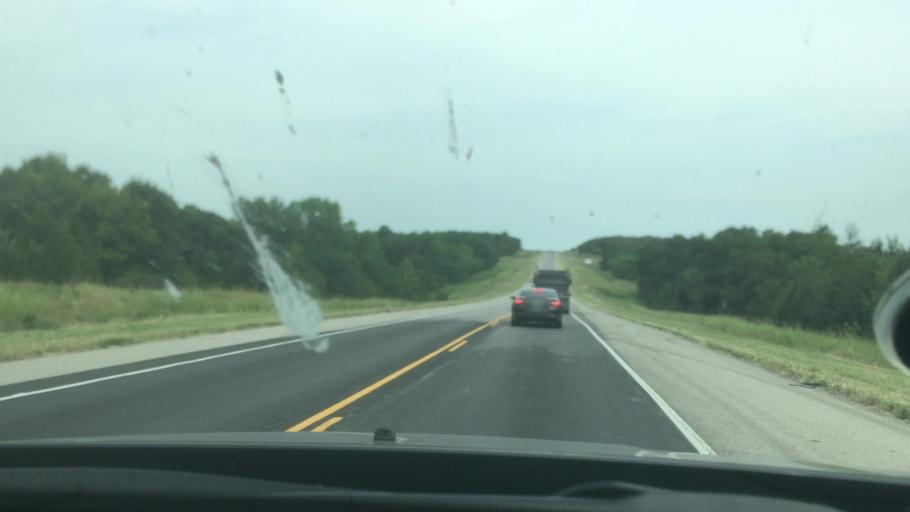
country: US
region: Oklahoma
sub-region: Pontotoc County
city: Ada
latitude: 34.6602
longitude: -96.5611
